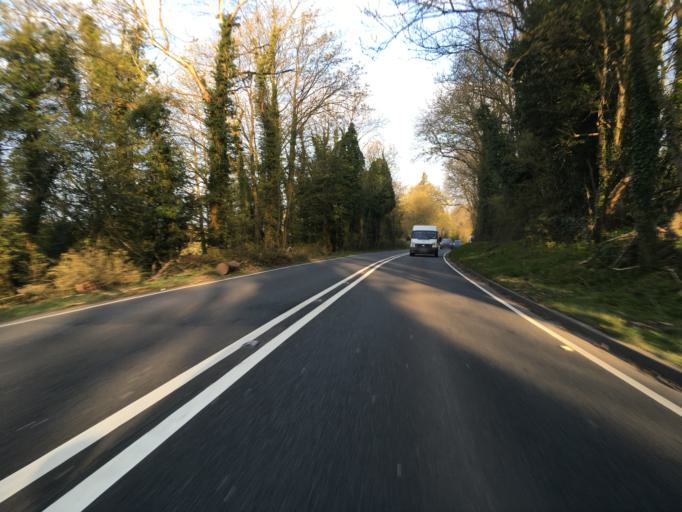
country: GB
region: England
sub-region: Gloucestershire
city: Charlton Kings
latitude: 51.8466
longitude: -2.0686
